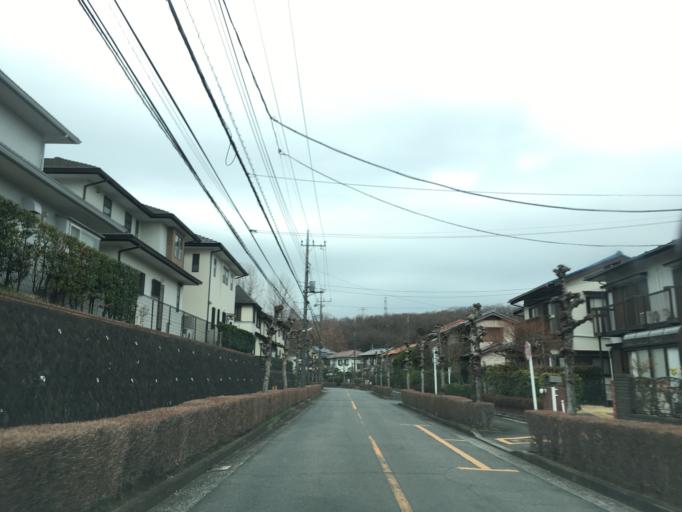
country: JP
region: Tokyo
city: Higashimurayama-shi
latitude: 35.7754
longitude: 139.4621
